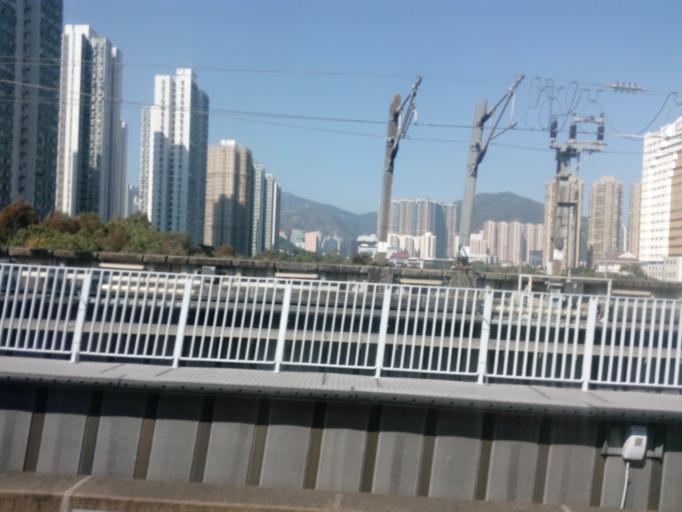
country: HK
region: Sha Tin
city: Sha Tin
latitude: 22.3863
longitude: 114.2070
